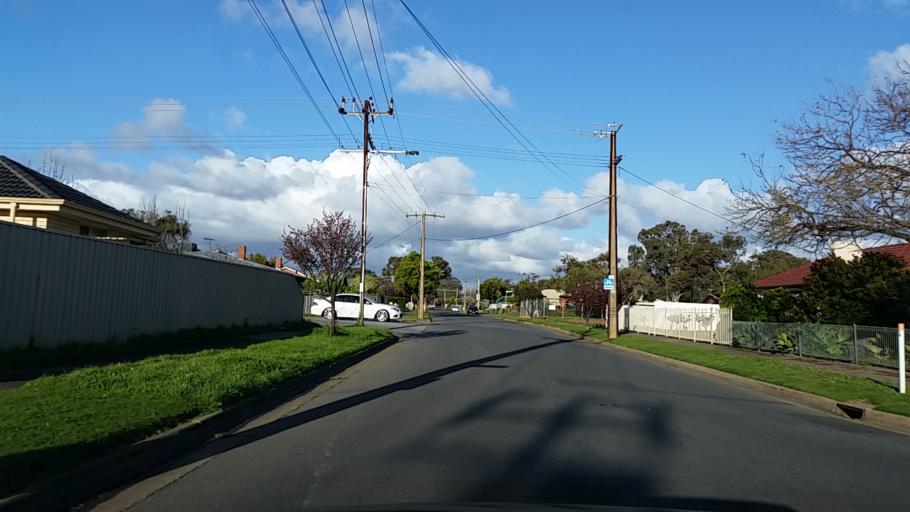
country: AU
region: South Australia
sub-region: Charles Sturt
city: Woodville West
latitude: -34.8879
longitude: 138.5258
